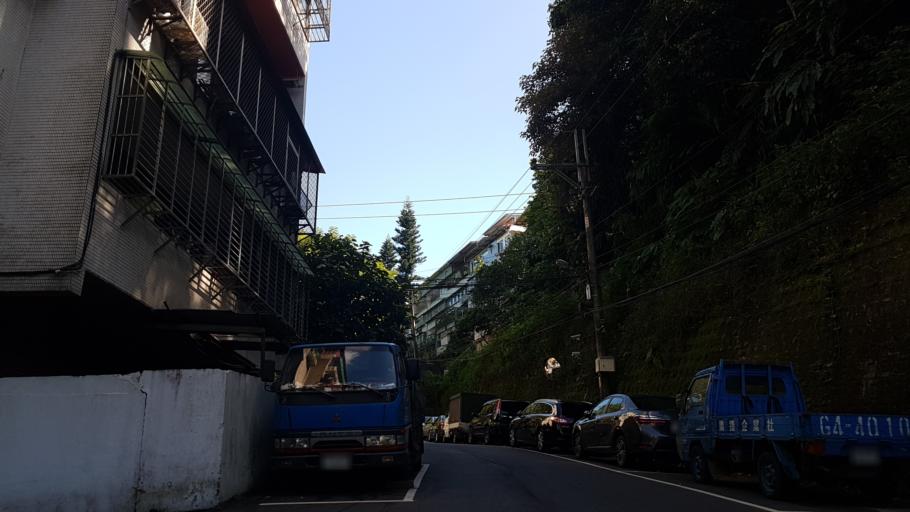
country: TW
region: Taipei
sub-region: Taipei
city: Banqiao
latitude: 24.9489
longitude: 121.5302
